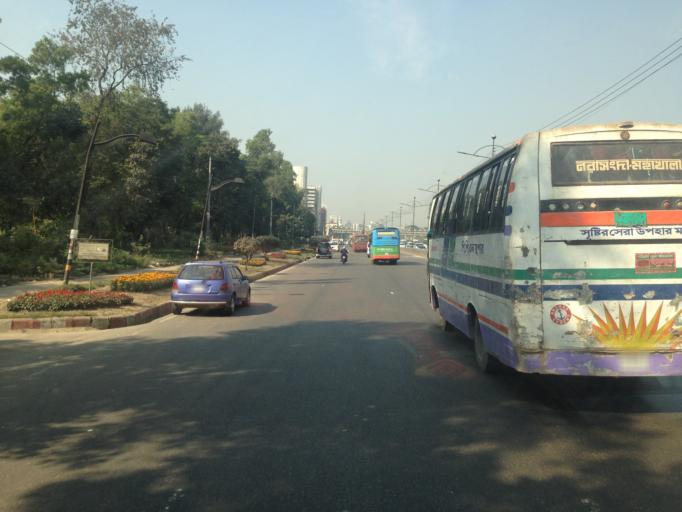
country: BD
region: Dhaka
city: Tungi
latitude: 23.8481
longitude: 90.4104
